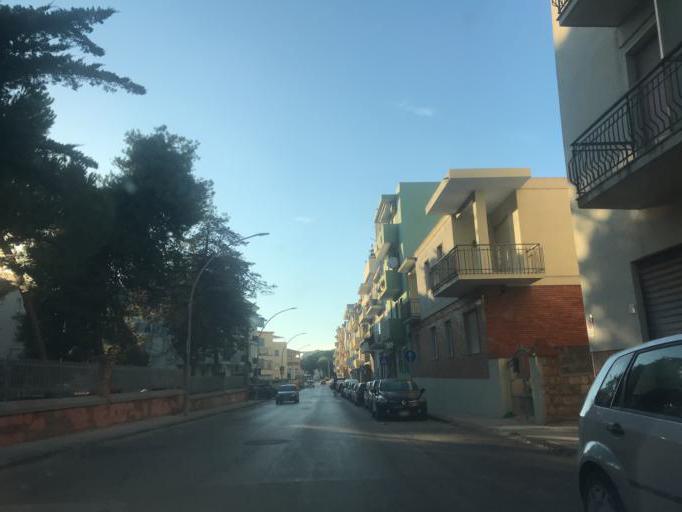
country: IT
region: Sardinia
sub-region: Provincia di Sassari
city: Alghero
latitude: 40.5712
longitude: 8.3245
